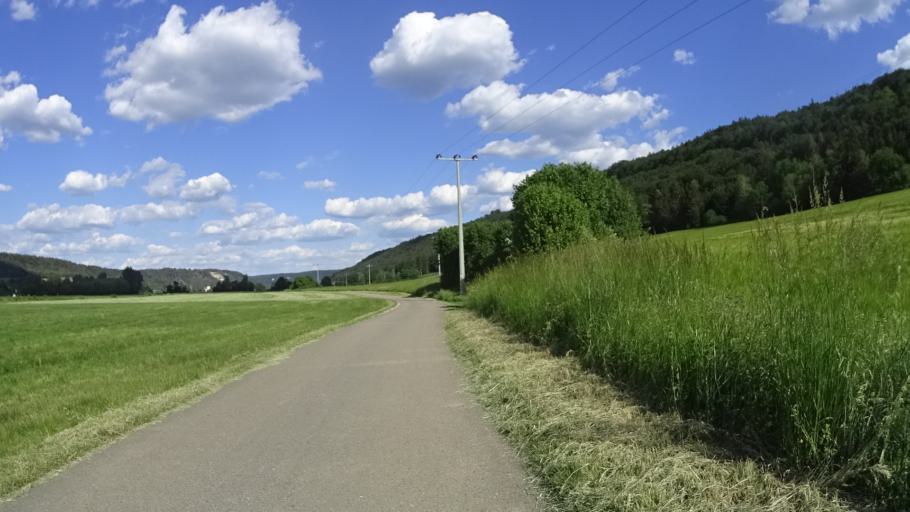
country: DE
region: Bavaria
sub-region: Upper Bavaria
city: Denkendorf
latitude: 49.0195
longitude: 11.4891
